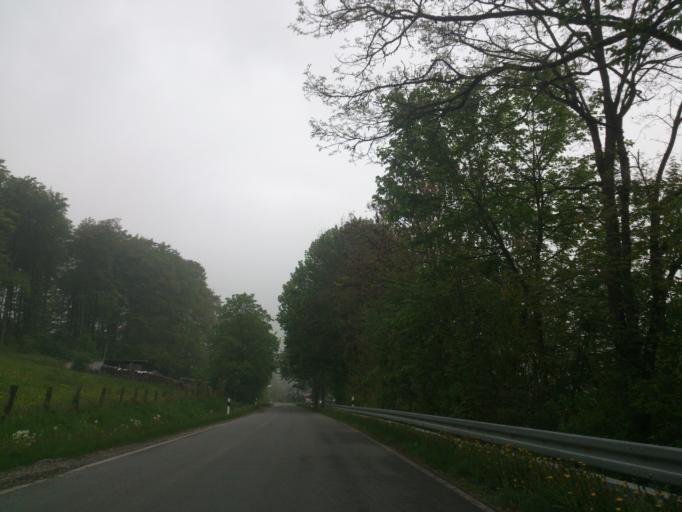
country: DE
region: North Rhine-Westphalia
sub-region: Regierungsbezirk Detmold
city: Willebadessen
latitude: 51.6695
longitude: 9.0094
